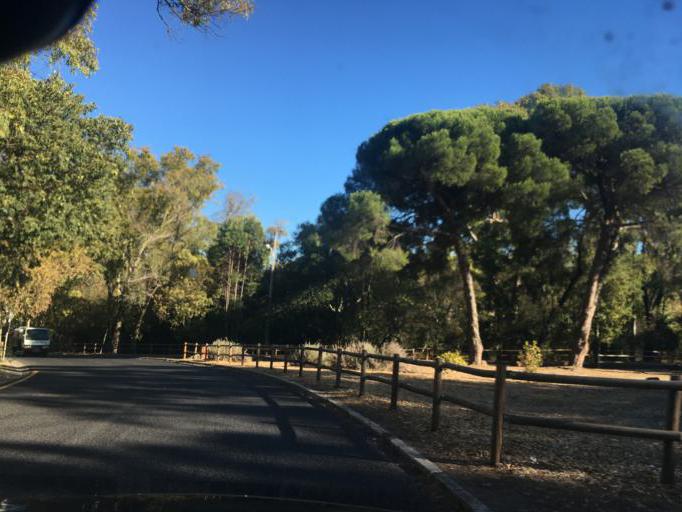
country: PT
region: Lisbon
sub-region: Oeiras
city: Alges
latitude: 38.7198
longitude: -9.1852
